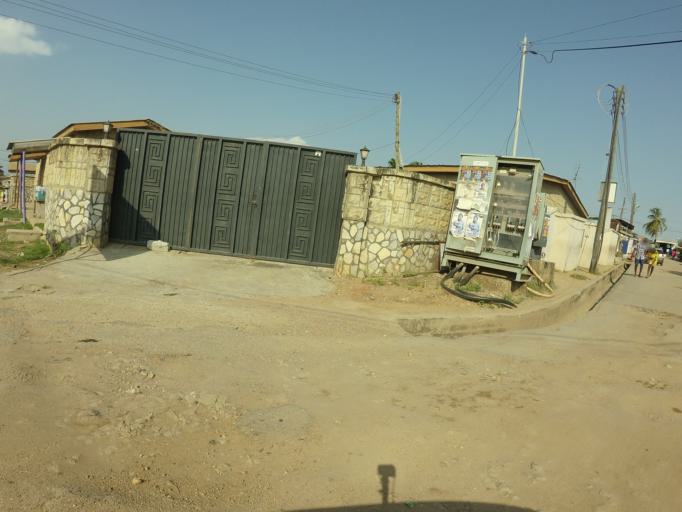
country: GH
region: Greater Accra
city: Dome
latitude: 5.6128
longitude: -0.2439
